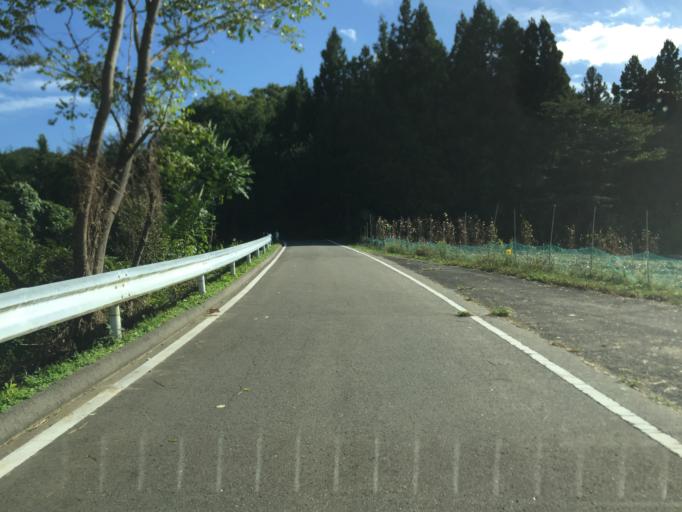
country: JP
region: Fukushima
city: Yanagawamachi-saiwaicho
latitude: 37.8527
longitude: 140.6680
